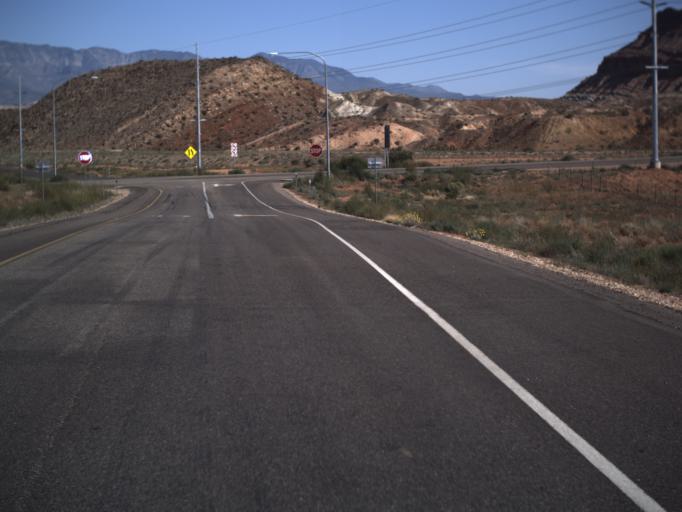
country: US
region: Utah
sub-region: Washington County
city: Washington
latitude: 37.0580
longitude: -113.4854
